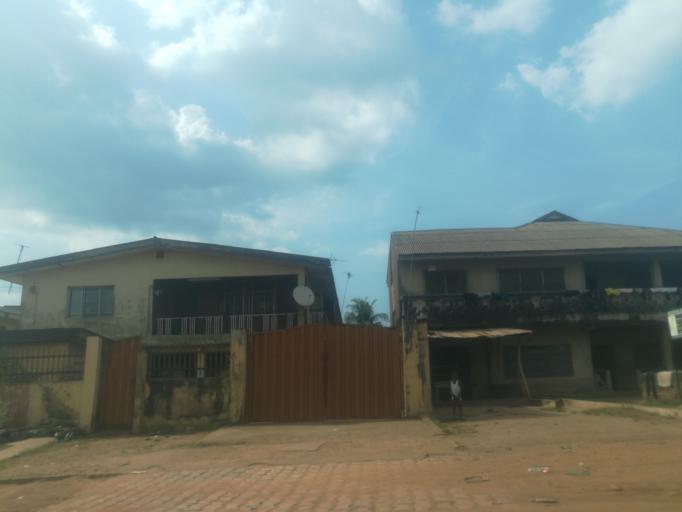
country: NG
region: Ogun
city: Abeokuta
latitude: 7.1174
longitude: 3.3173
